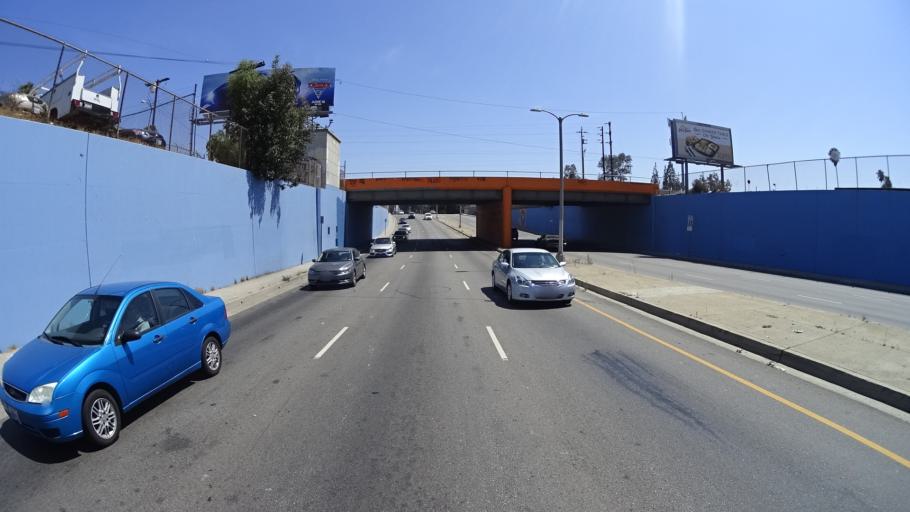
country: US
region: California
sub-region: Los Angeles County
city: Van Nuys
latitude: 34.2085
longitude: -118.4310
